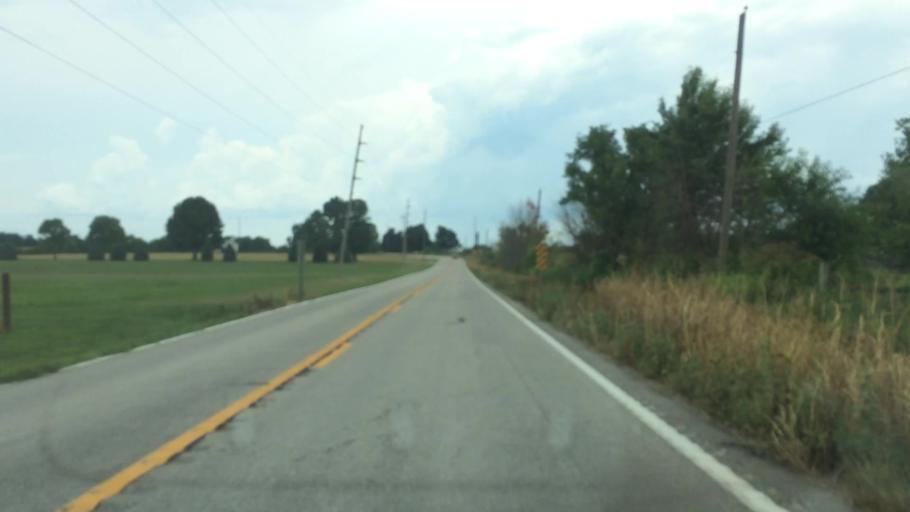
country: US
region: Missouri
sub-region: Greene County
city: Strafford
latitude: 37.2492
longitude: -93.1354
